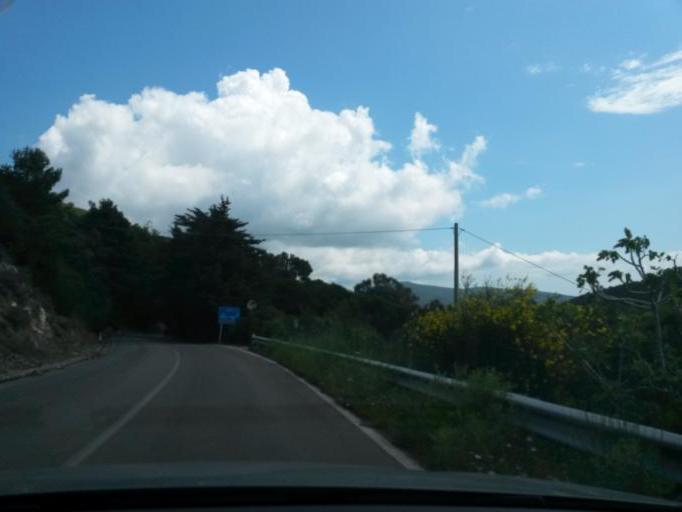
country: IT
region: Tuscany
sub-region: Provincia di Livorno
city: Marina di Campo
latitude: 42.7368
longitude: 10.2018
